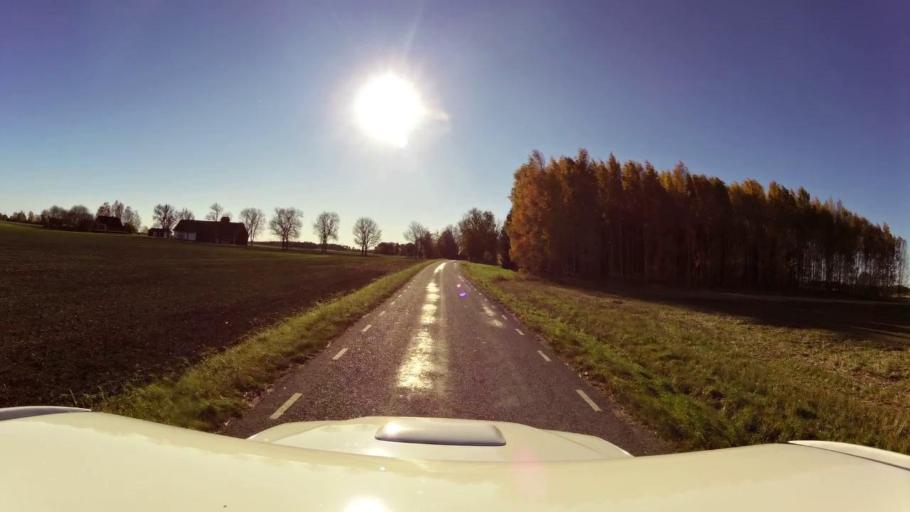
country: SE
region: OEstergoetland
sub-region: Linkopings Kommun
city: Ljungsbro
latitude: 58.4855
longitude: 15.4180
